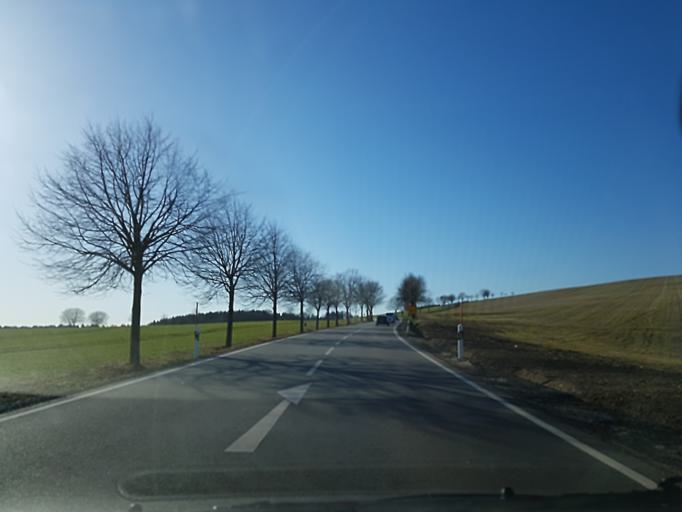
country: DE
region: Saxony
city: Oederan
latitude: 50.8615
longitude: 13.1494
